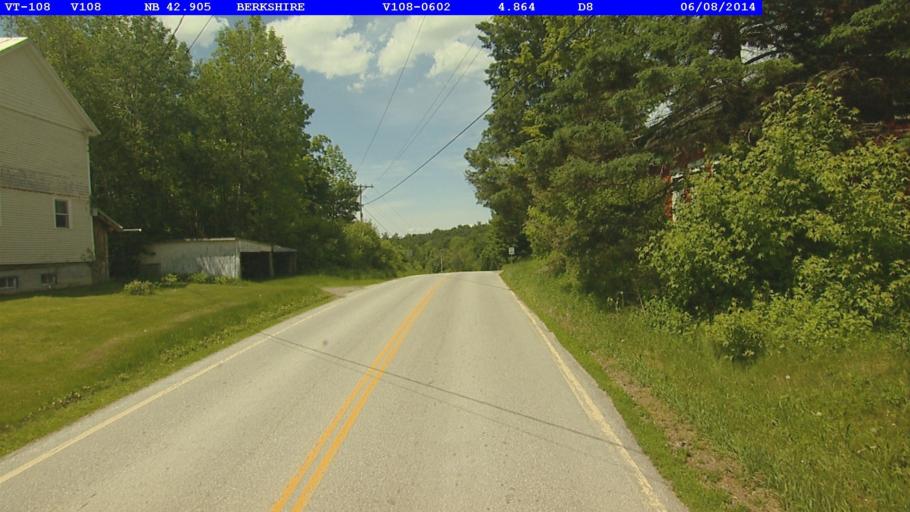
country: US
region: Vermont
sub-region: Franklin County
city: Enosburg Falls
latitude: 44.9901
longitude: -72.8135
